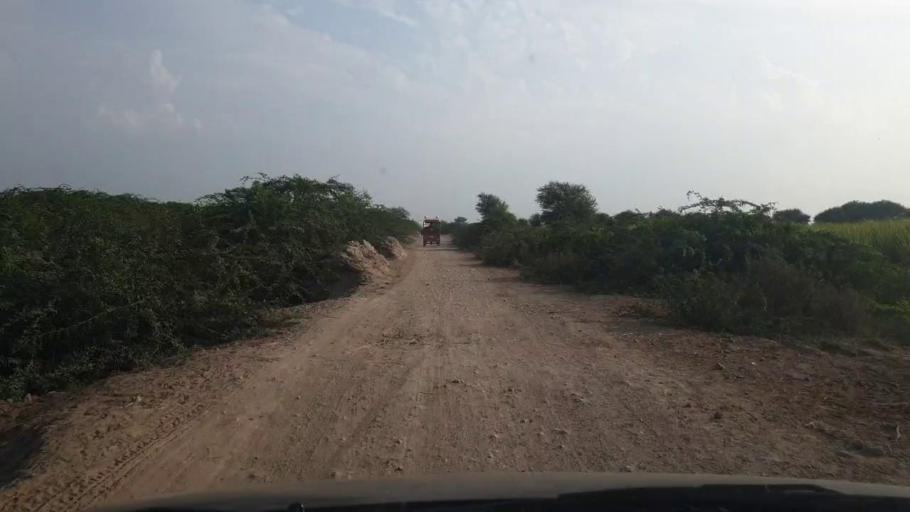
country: PK
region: Sindh
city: Badin
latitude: 24.5666
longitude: 68.6672
